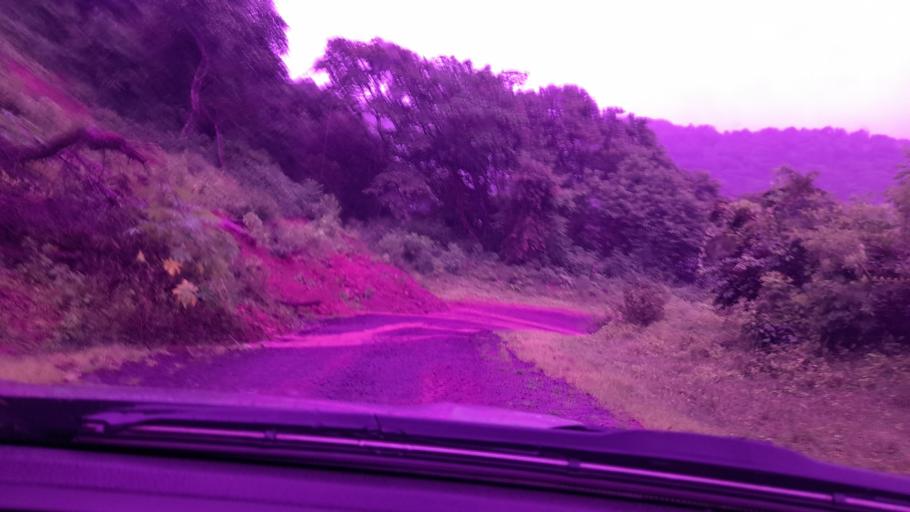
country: ET
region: Oromiya
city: Metu
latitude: 8.4805
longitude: 35.6422
